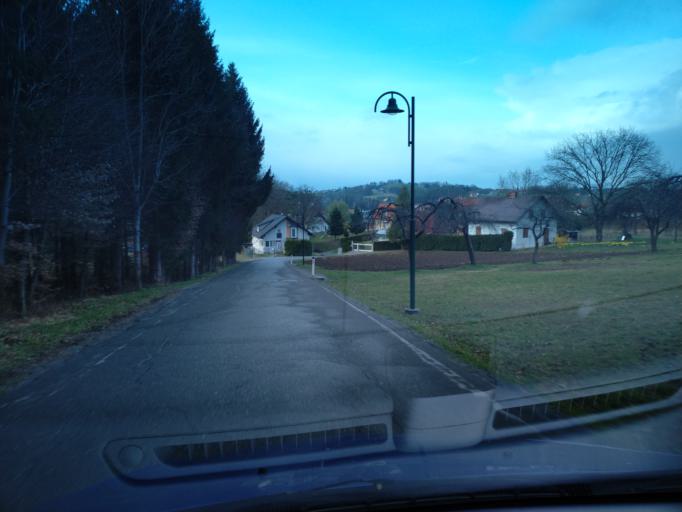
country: AT
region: Styria
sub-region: Politischer Bezirk Deutschlandsberg
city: Pitschgau
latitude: 46.6900
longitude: 15.2624
